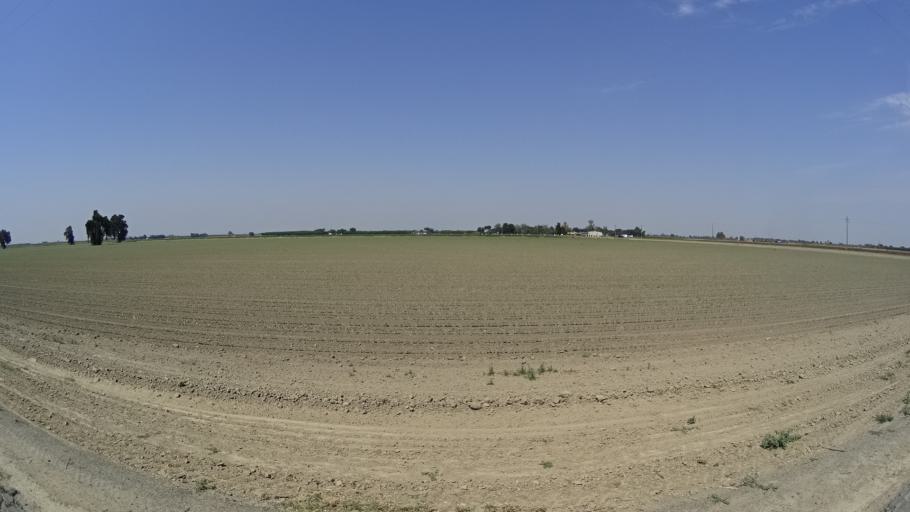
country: US
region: California
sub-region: Kings County
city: Armona
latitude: 36.3707
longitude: -119.7450
